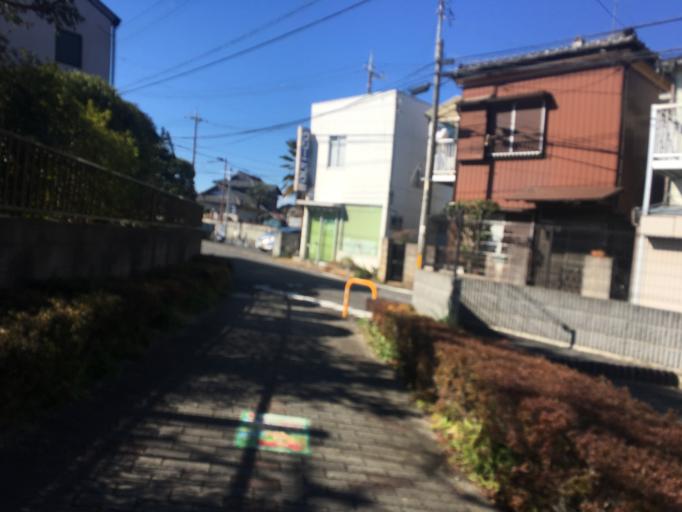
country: JP
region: Saitama
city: Shiki
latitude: 35.8103
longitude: 139.5715
